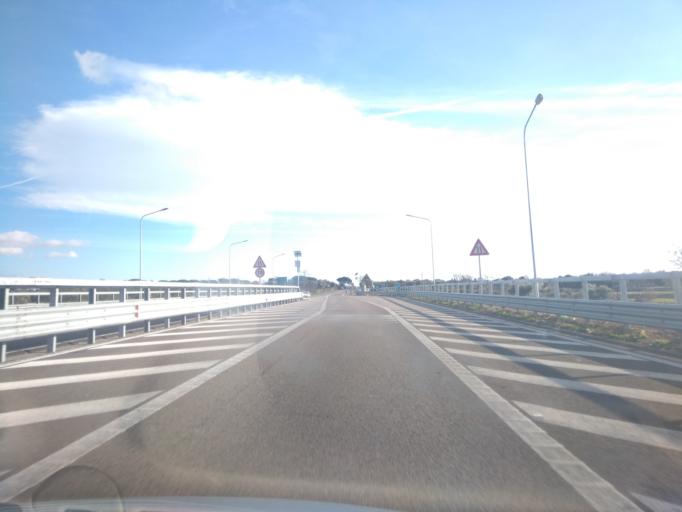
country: IT
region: Apulia
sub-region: Provincia di Bari
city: Gioia del Colle
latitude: 40.7551
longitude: 16.9599
